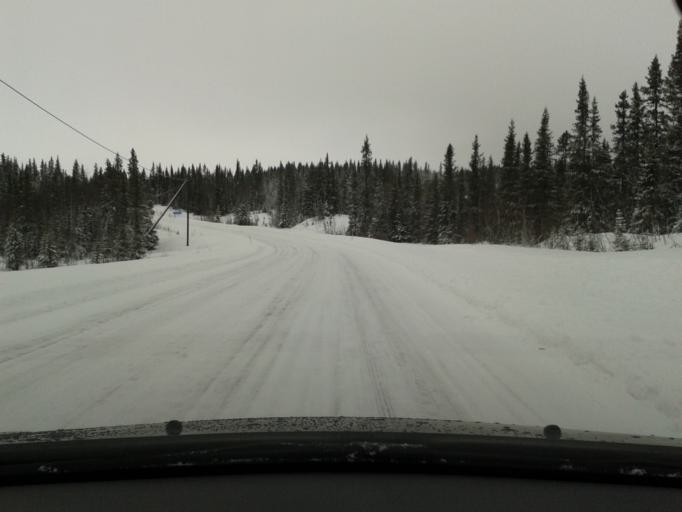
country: SE
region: Vaesterbotten
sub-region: Vilhelmina Kommun
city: Sjoberg
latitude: 65.1814
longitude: 15.8825
